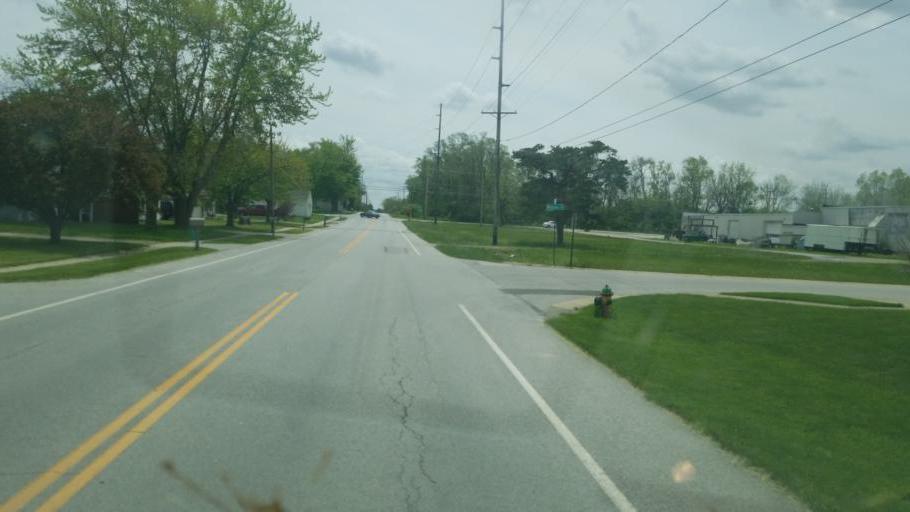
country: US
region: Ohio
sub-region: Sandusky County
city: Stony Prairie
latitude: 41.3506
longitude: -83.1463
